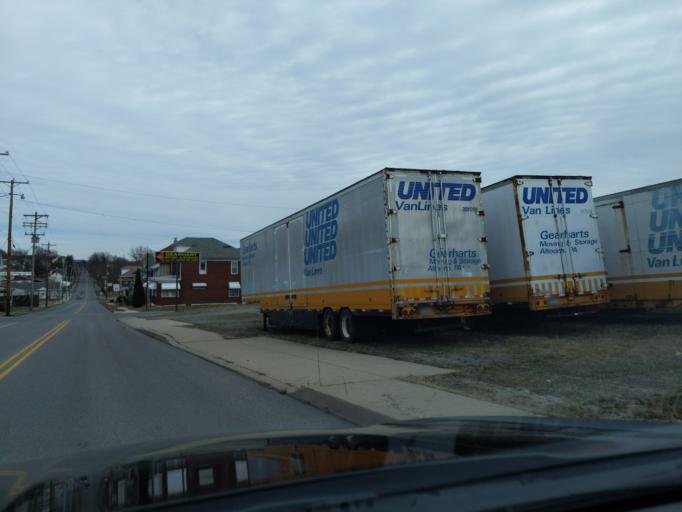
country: US
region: Pennsylvania
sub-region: Blair County
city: Greenwood
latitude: 40.5398
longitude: -78.3801
